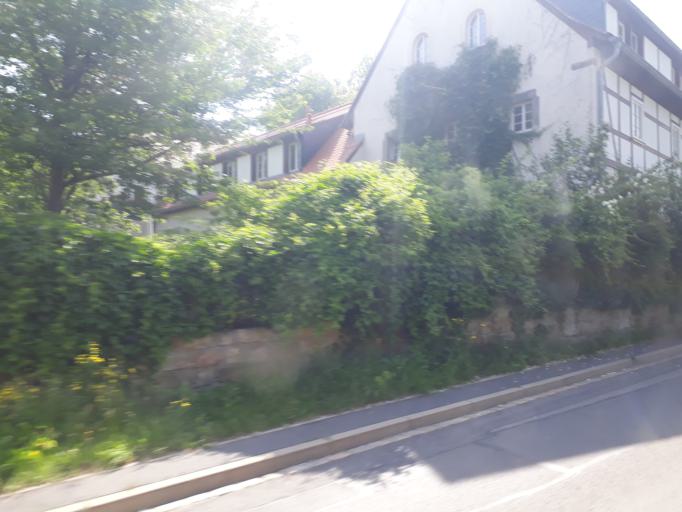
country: DE
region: Saxony
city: Radeberg
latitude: 51.0588
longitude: 13.8588
